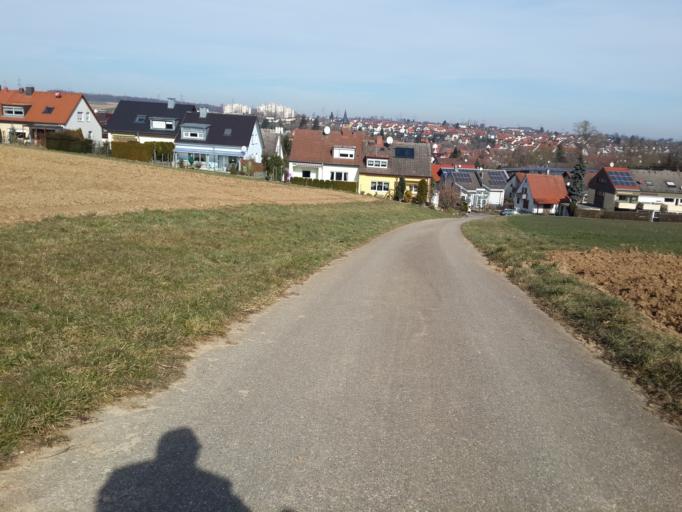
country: DE
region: Baden-Wuerttemberg
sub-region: Regierungsbezirk Stuttgart
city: Heilbronn
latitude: 49.1529
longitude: 9.1694
